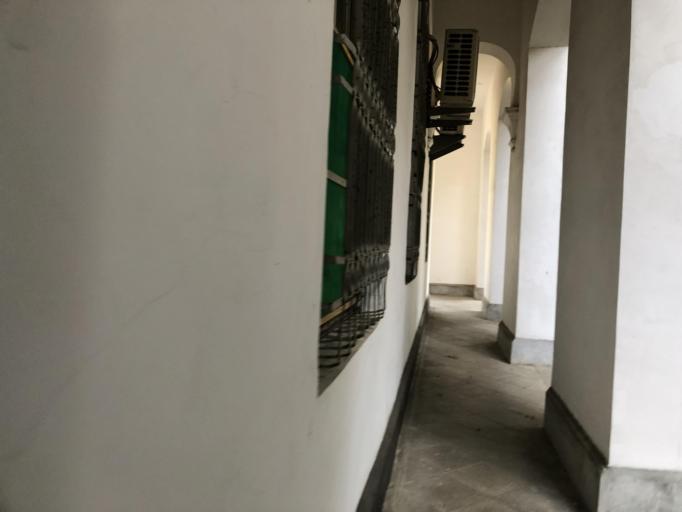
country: TW
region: Taiwan
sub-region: Tainan
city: Tainan
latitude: 22.9992
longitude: 120.2176
